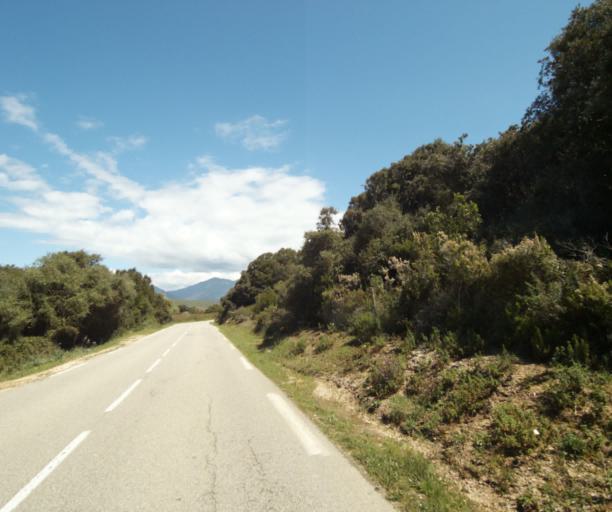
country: FR
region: Corsica
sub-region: Departement de la Corse-du-Sud
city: Propriano
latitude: 41.6484
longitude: 8.8777
